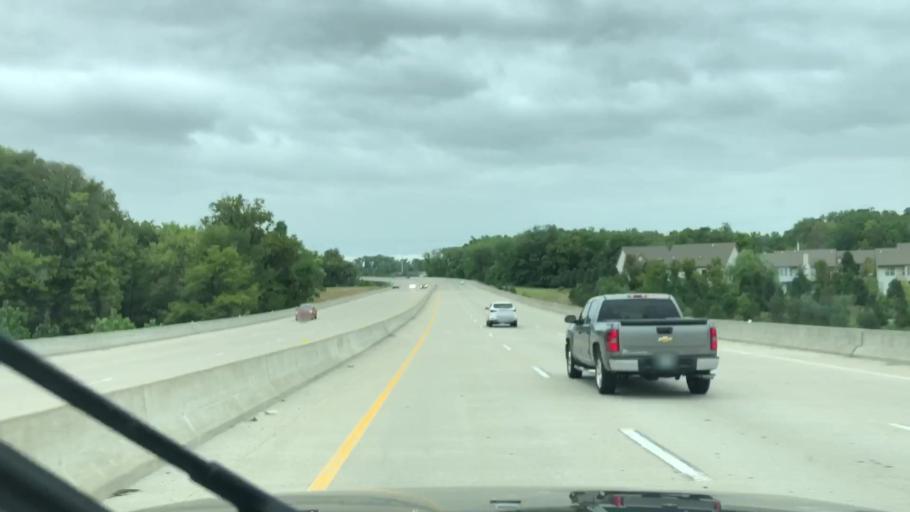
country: US
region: Missouri
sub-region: Saint Louis County
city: Maryland Heights
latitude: 38.6848
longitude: -90.4942
